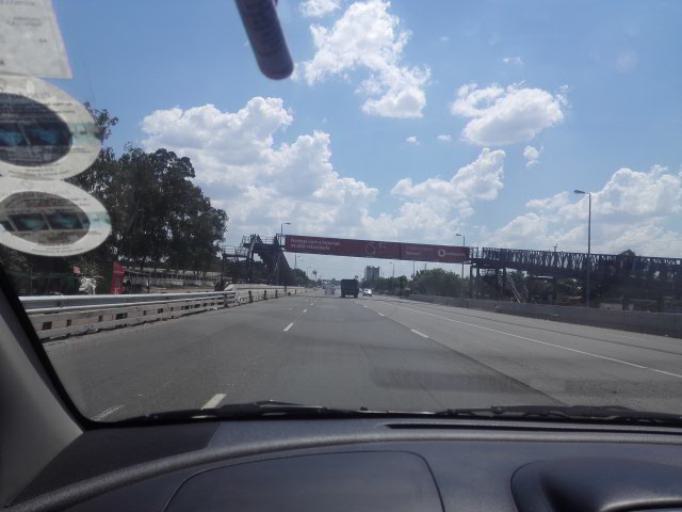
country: MZ
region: Maputo
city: Matola
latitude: -25.9491
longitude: 32.4716
